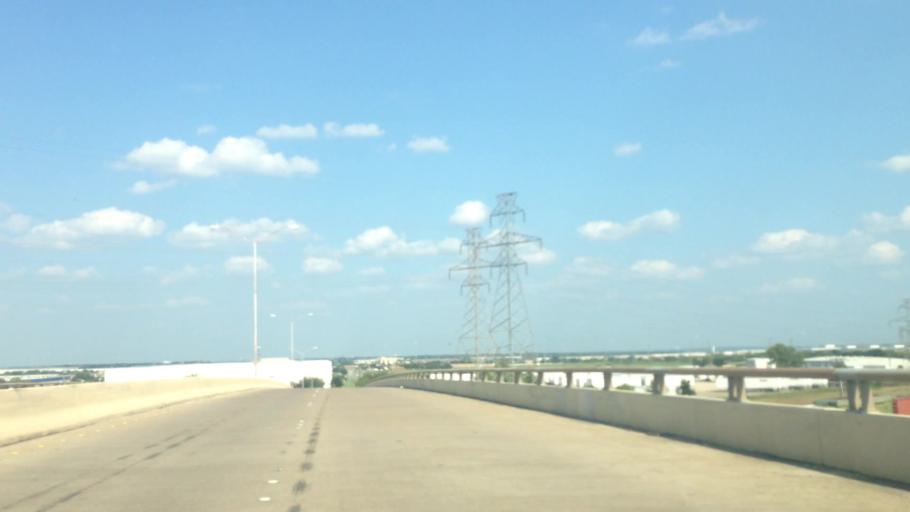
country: US
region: Texas
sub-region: Tarrant County
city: Blue Mound
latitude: 32.8248
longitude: -97.3324
